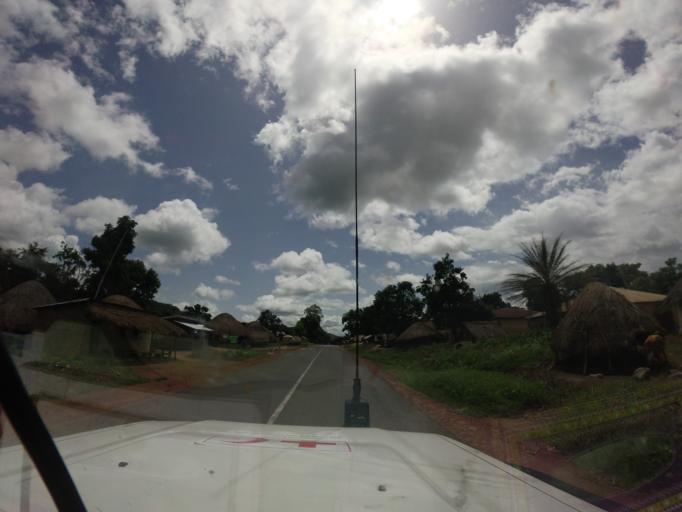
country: SL
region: Northern Province
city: Bindi
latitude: 10.1791
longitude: -11.7216
